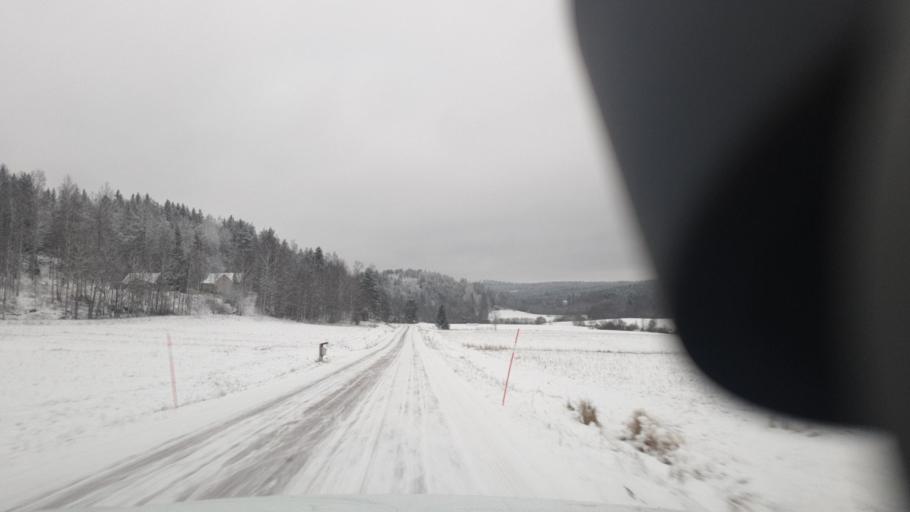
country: NO
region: Ostfold
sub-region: Romskog
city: Romskog
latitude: 59.7060
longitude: 12.0759
